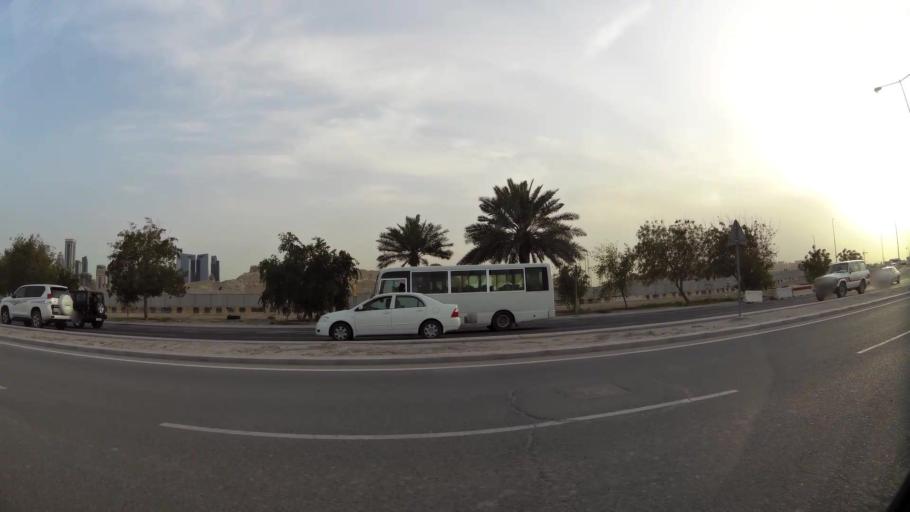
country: QA
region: Baladiyat ad Dawhah
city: Doha
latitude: 25.3450
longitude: 51.5224
